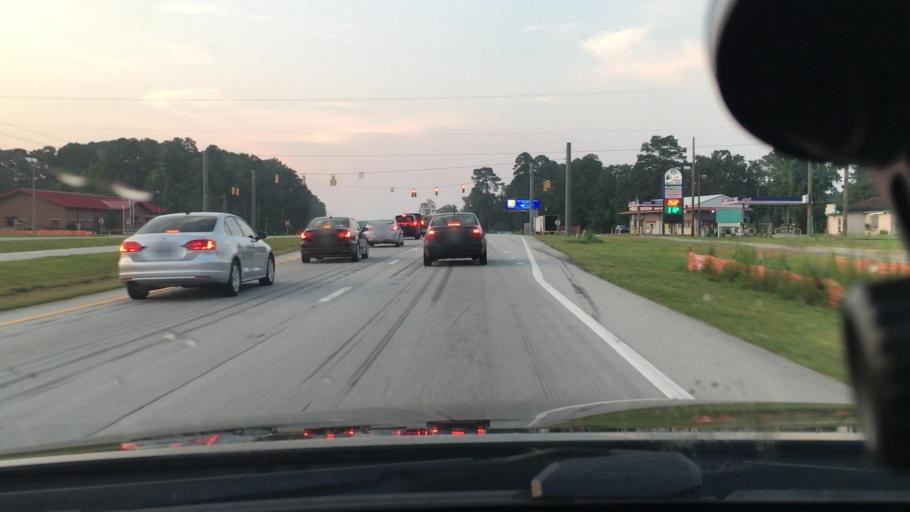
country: US
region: North Carolina
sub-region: Craven County
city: Neuse Forest
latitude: 34.9281
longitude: -76.9481
